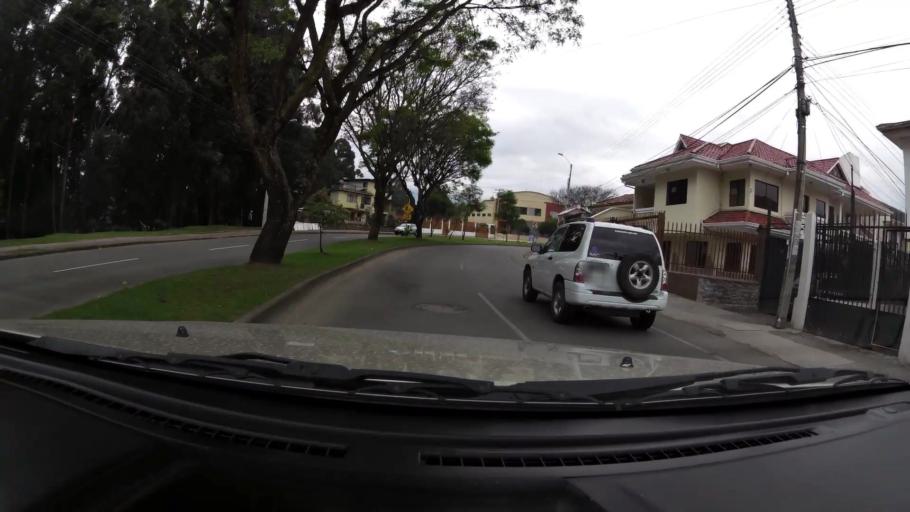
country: EC
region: Azuay
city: Cuenca
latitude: -2.9061
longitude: -79.0245
